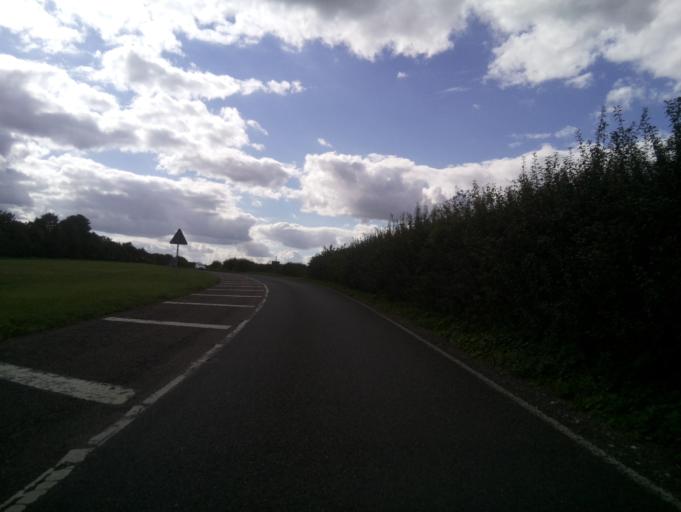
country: GB
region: England
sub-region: Hampshire
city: Abbotts Ann
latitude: 51.1187
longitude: -1.5062
